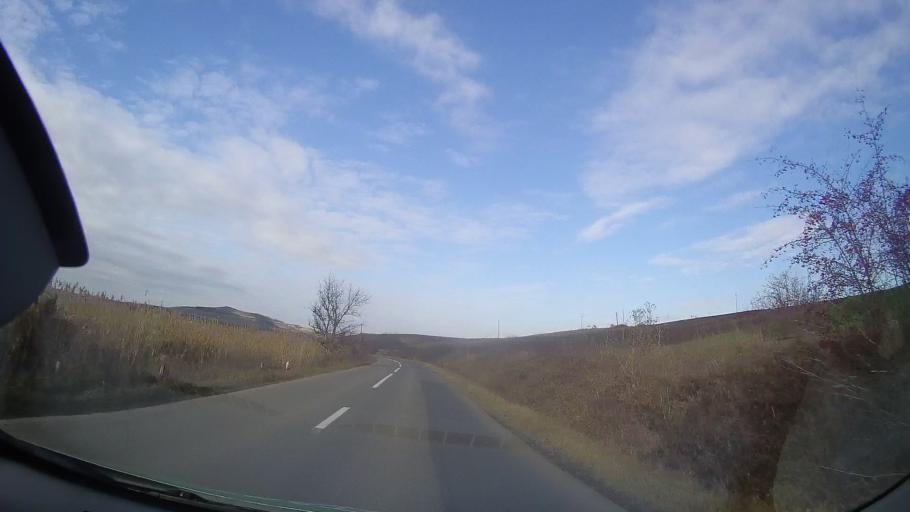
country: RO
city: Barza
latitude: 46.5639
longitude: 24.0971
